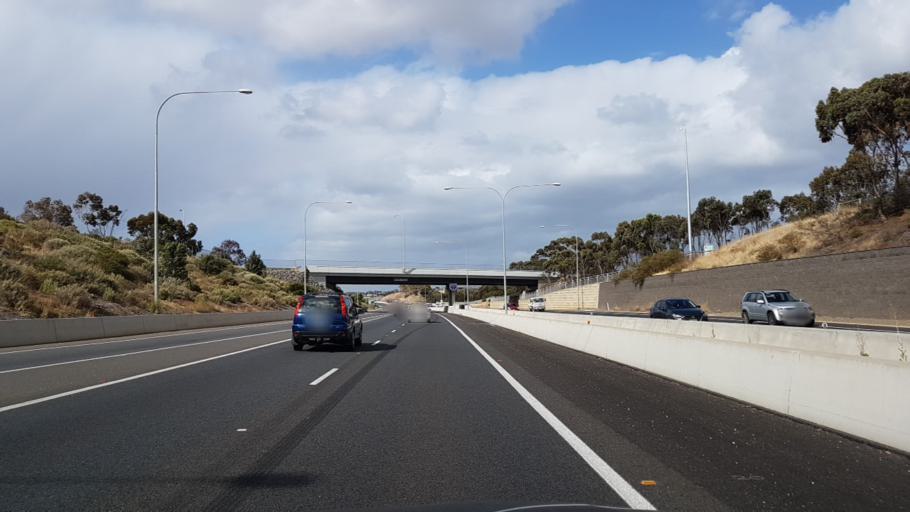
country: AU
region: South Australia
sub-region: Onkaparinga
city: Reynella
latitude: -35.1018
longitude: 138.5133
